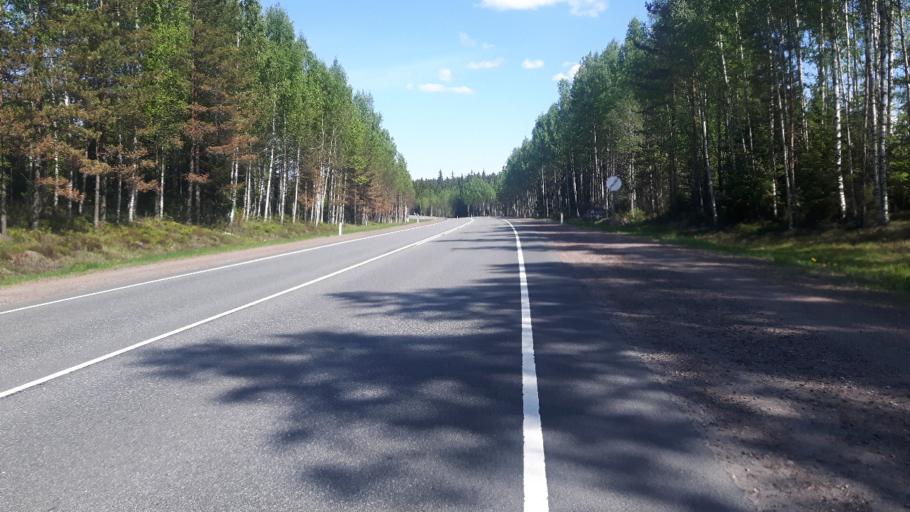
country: RU
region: Leningrad
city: Vysotsk
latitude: 60.6406
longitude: 28.3029
